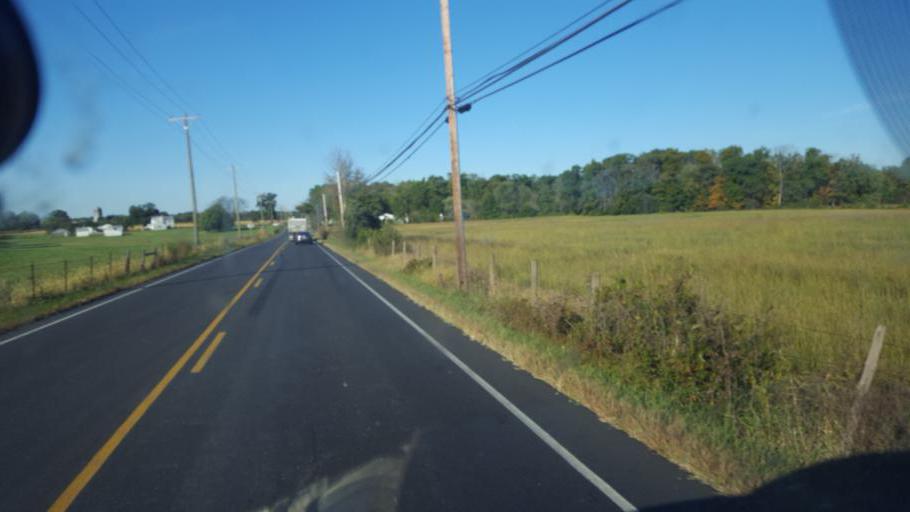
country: US
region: Virginia
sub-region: Prince William County
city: Nokesville
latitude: 38.6398
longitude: -77.6619
